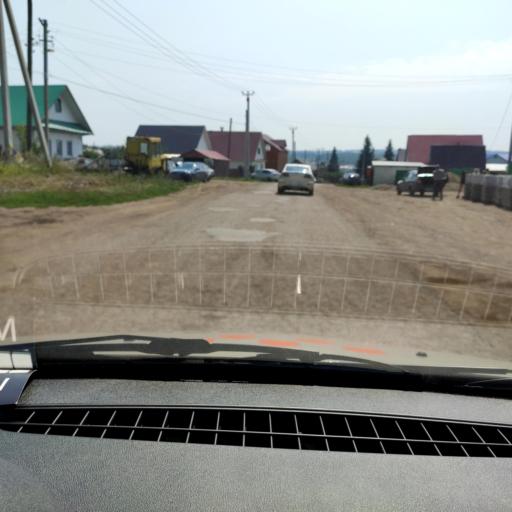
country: RU
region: Bashkortostan
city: Iglino
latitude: 54.8424
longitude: 56.4063
